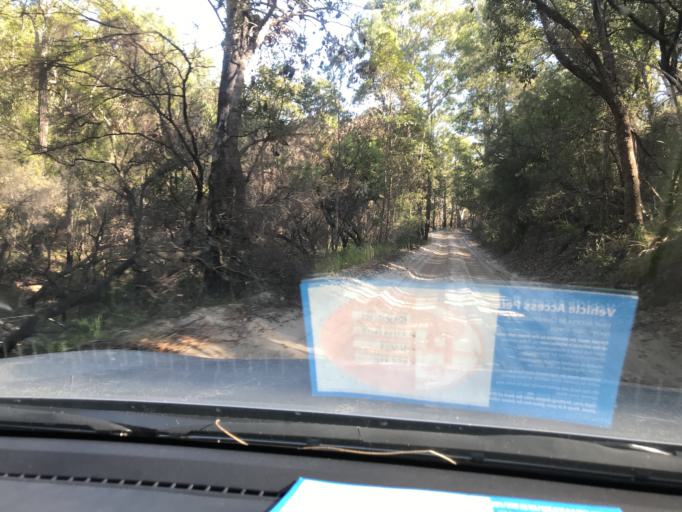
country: AU
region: Queensland
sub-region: Fraser Coast
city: Urangan
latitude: -25.5033
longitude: 153.1080
